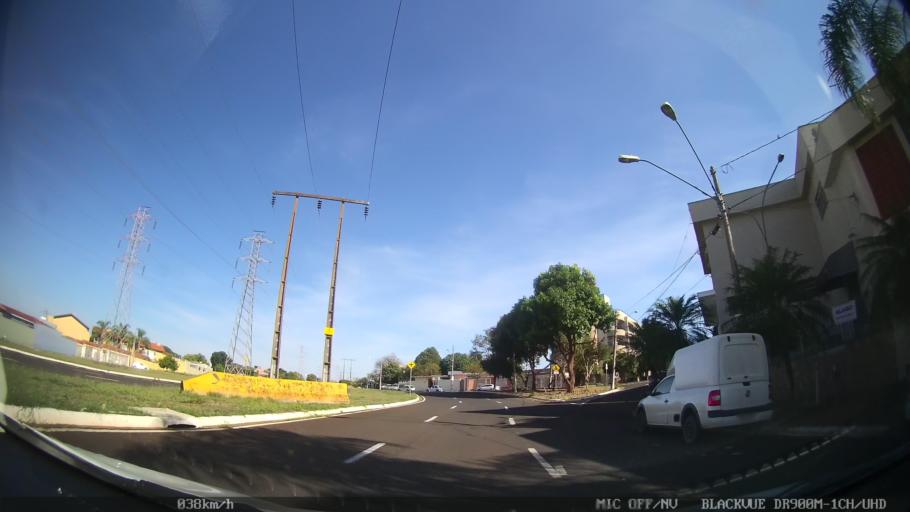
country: BR
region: Sao Paulo
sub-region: Ribeirao Preto
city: Ribeirao Preto
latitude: -21.1808
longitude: -47.7829
